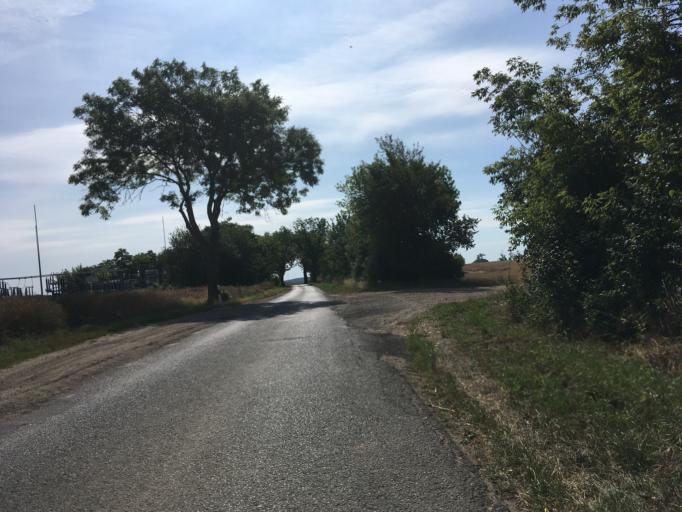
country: DE
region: Brandenburg
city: Gramzow
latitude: 53.2852
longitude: 14.0495
